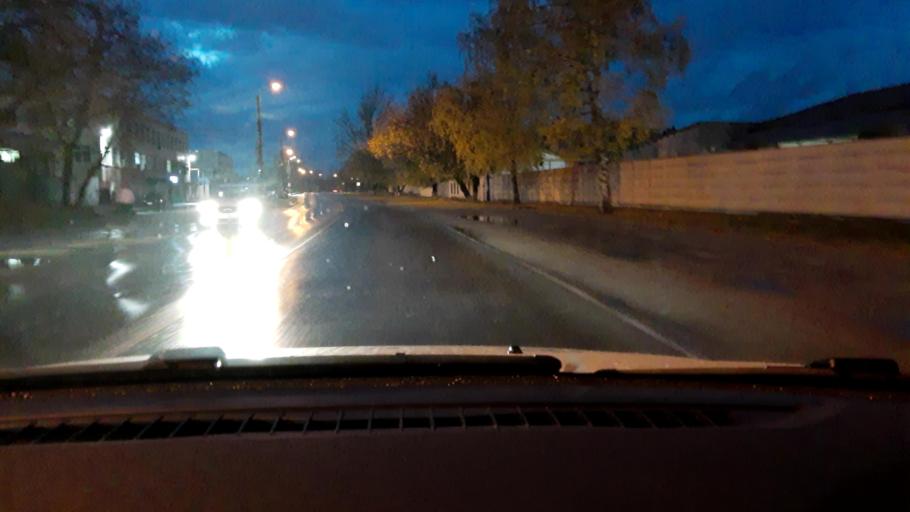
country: RU
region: Nizjnij Novgorod
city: Bor
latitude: 56.3452
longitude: 44.0876
